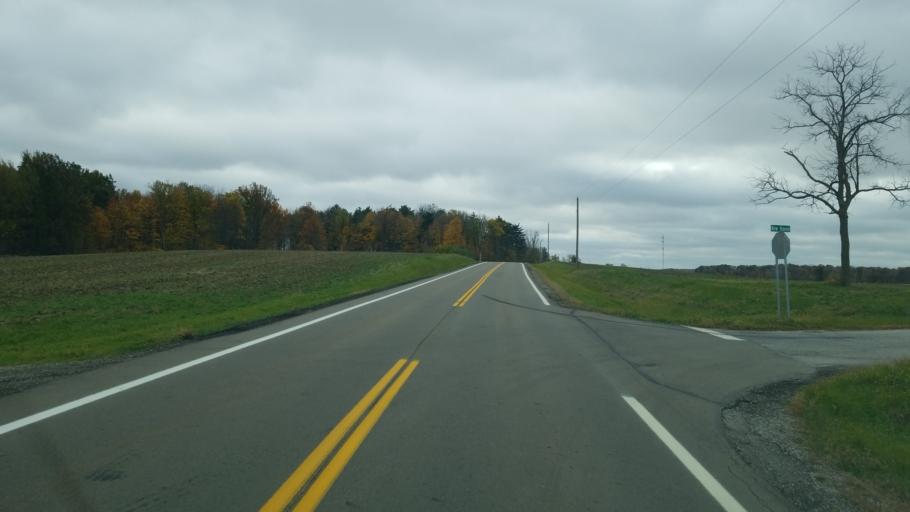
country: US
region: Ohio
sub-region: Richland County
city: Shelby
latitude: 40.9054
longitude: -82.7385
